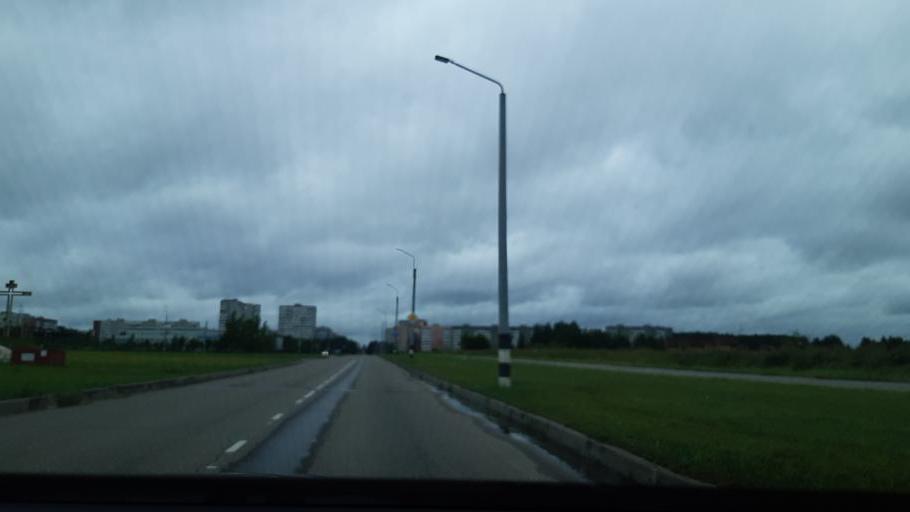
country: RU
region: Smolensk
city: Desnogorsk
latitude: 54.1420
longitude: 33.2793
